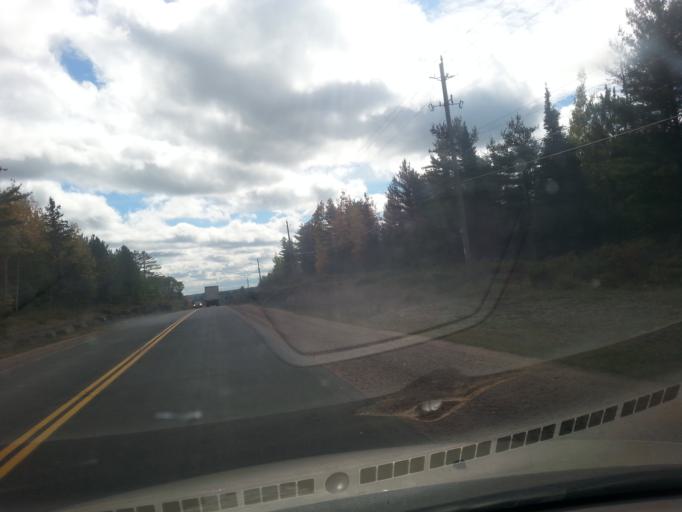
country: CA
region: Ontario
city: Pembroke
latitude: 45.7278
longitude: -77.0989
